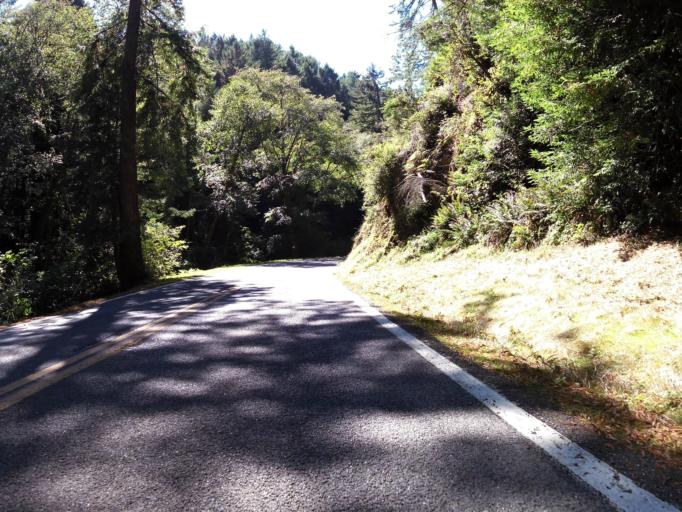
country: US
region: California
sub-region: Humboldt County
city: Redway
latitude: 39.7840
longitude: -123.8200
